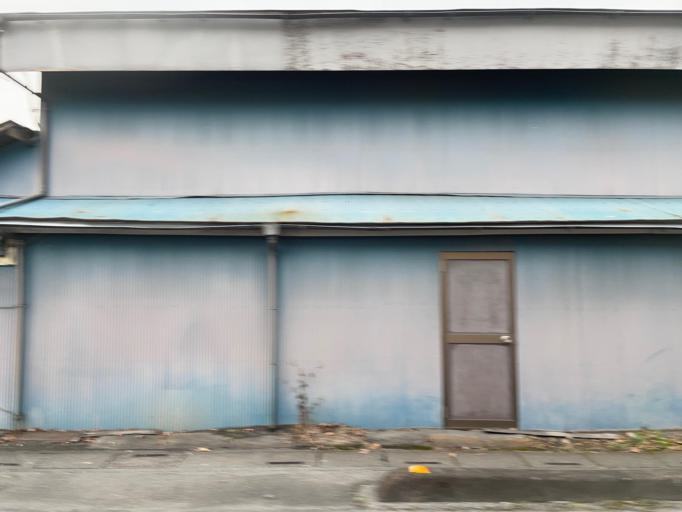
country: JP
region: Saitama
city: Yorii
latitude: 36.1190
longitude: 139.2003
